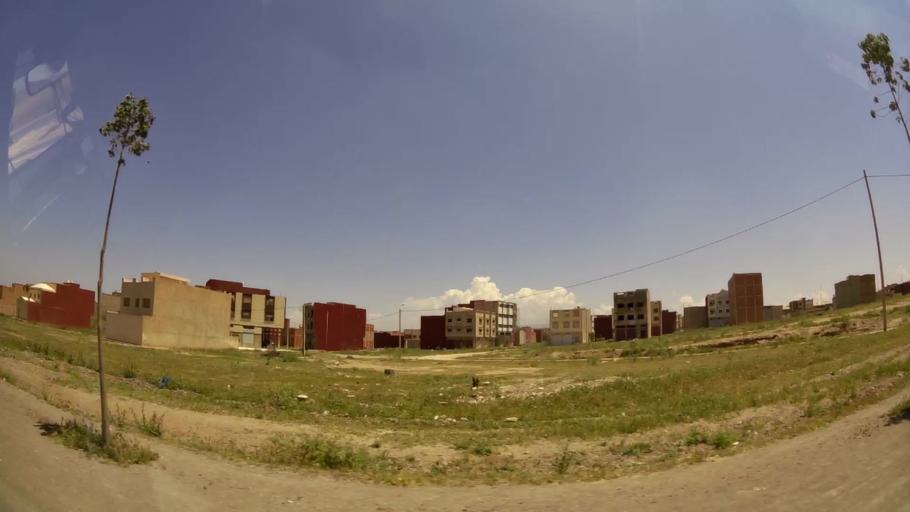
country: MA
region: Oriental
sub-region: Oujda-Angad
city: Oujda
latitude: 34.6625
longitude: -1.9539
